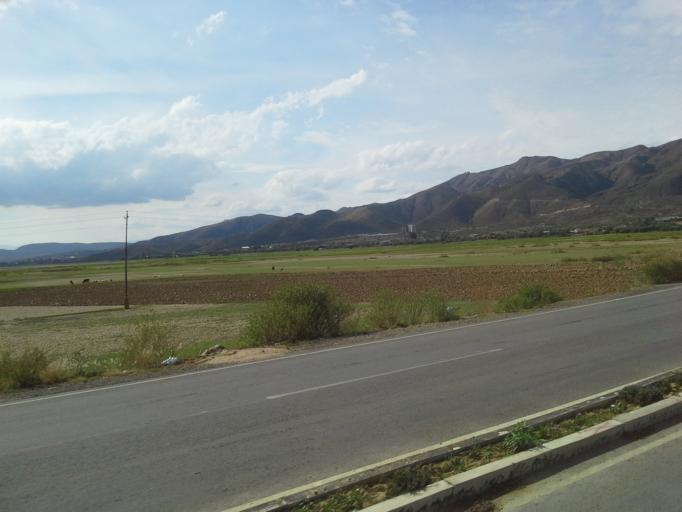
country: BO
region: Cochabamba
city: Tarata
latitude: -17.5566
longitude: -66.0079
